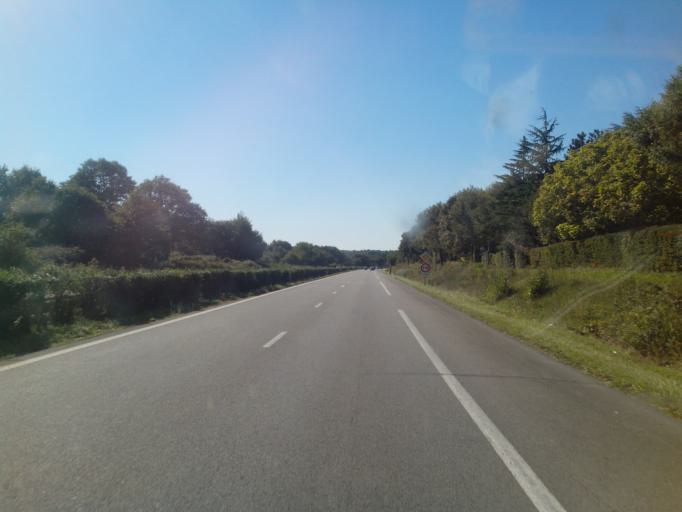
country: FR
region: Pays de la Loire
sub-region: Departement de la Loire-Atlantique
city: Sautron
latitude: 47.2555
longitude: -1.6474
